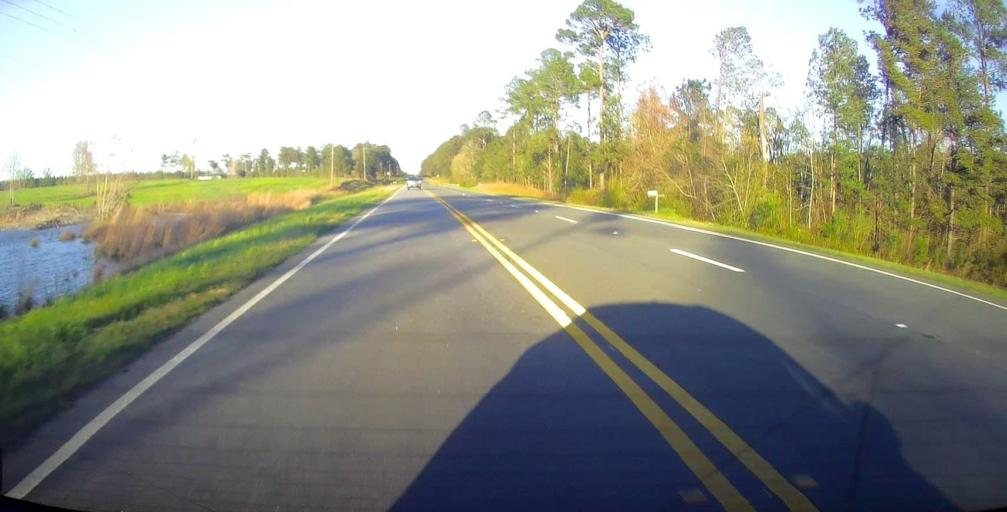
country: US
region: Georgia
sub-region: Wilcox County
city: Abbeville
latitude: 31.9725
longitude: -83.3688
